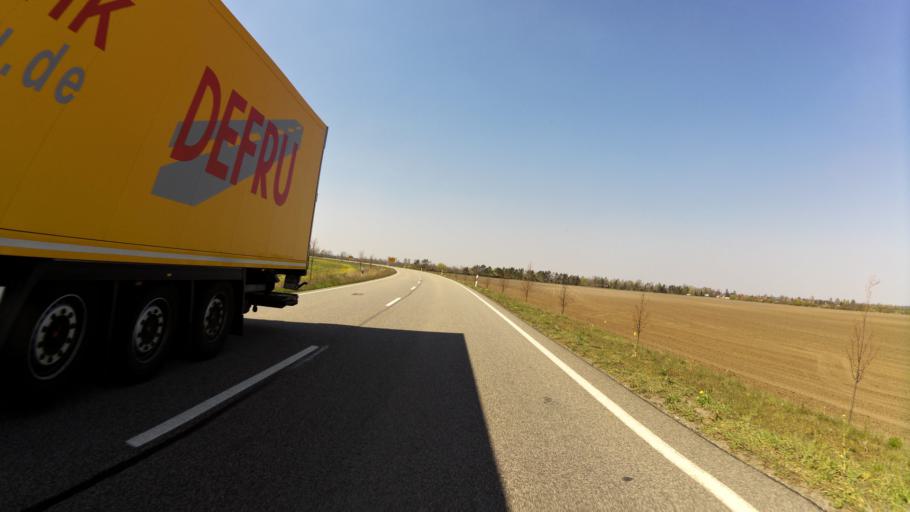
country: DE
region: Saxony-Anhalt
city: Oebisfelde
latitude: 52.4468
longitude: 10.9857
